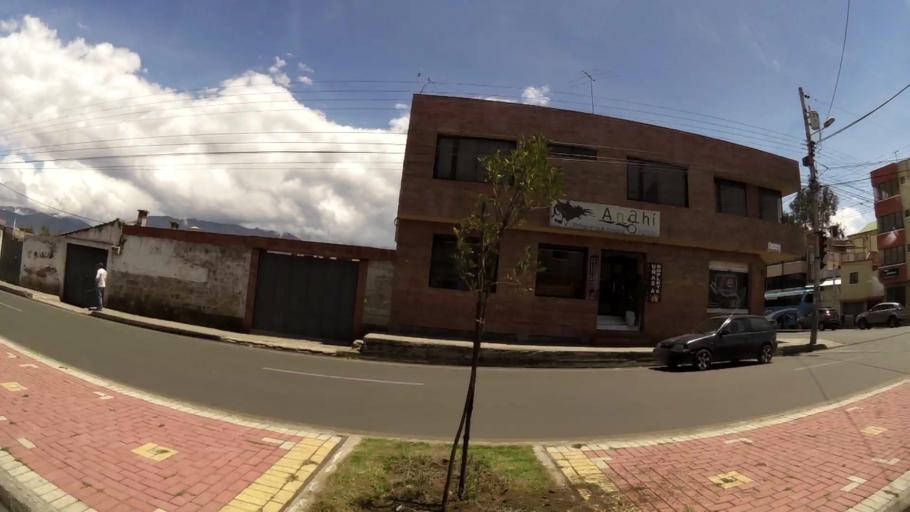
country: EC
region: Chimborazo
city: Riobamba
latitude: -1.6791
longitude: -78.6411
